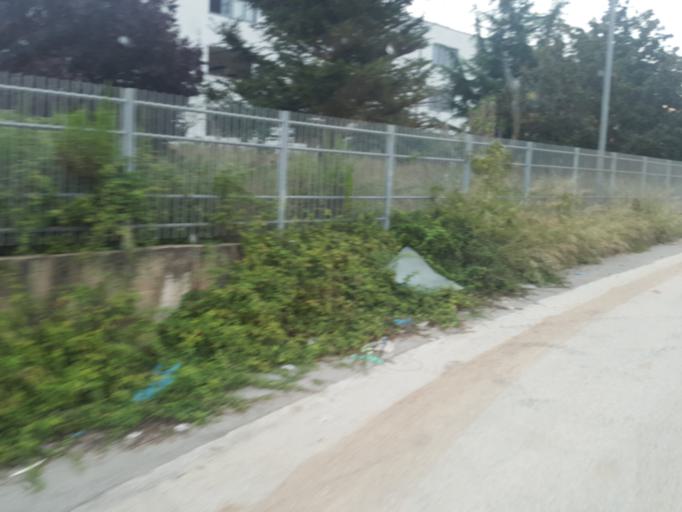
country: IT
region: Campania
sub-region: Provincia di Caserta
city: Pignataro Maggiore
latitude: 41.1748
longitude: 14.1507
